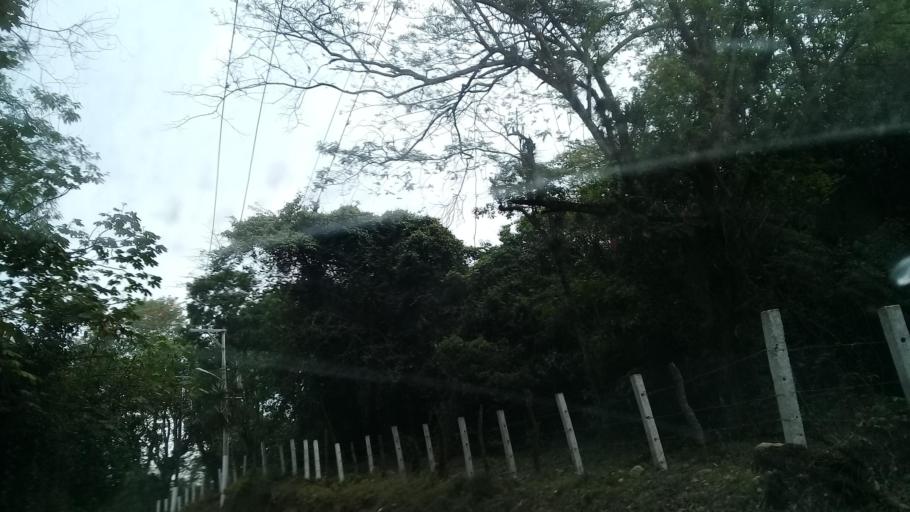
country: MX
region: Veracruz
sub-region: Xalapa
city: Fraccionamiento las Fuentes
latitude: 19.4967
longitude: -96.8989
